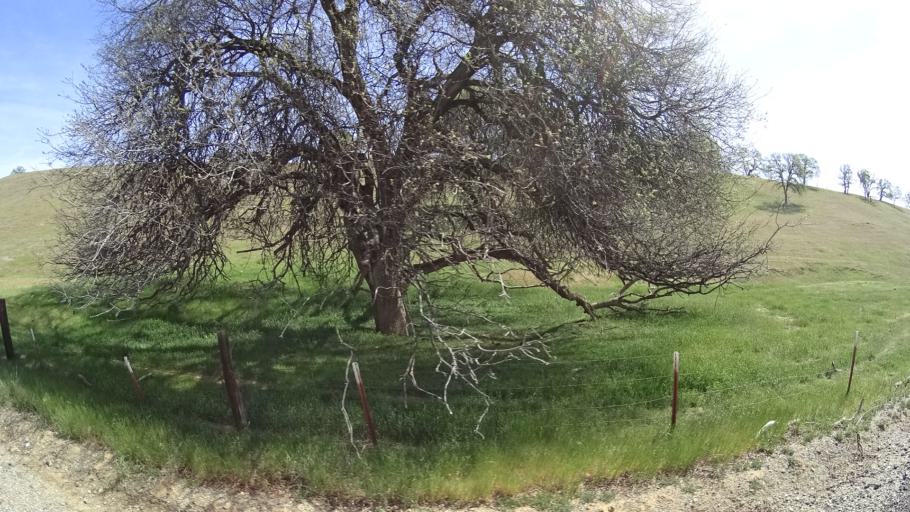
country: US
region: California
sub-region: Glenn County
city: Willows
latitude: 39.5586
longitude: -122.4388
